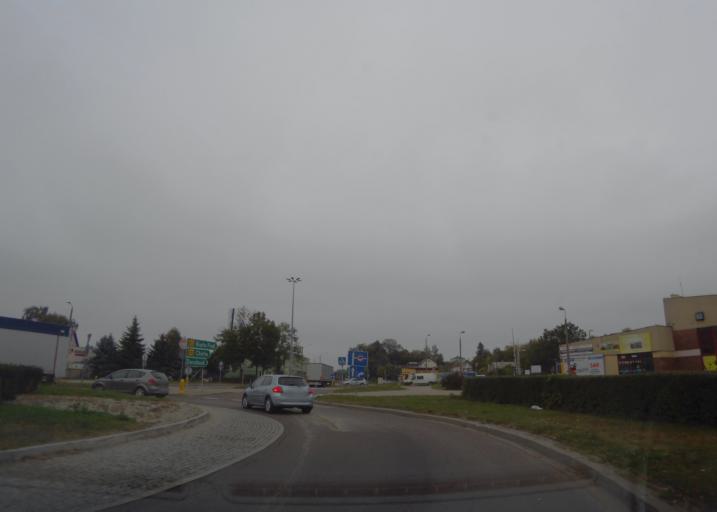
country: PL
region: Lublin Voivodeship
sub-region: Powiat krasnostawski
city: Krasnystaw
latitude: 50.9853
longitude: 23.1819
